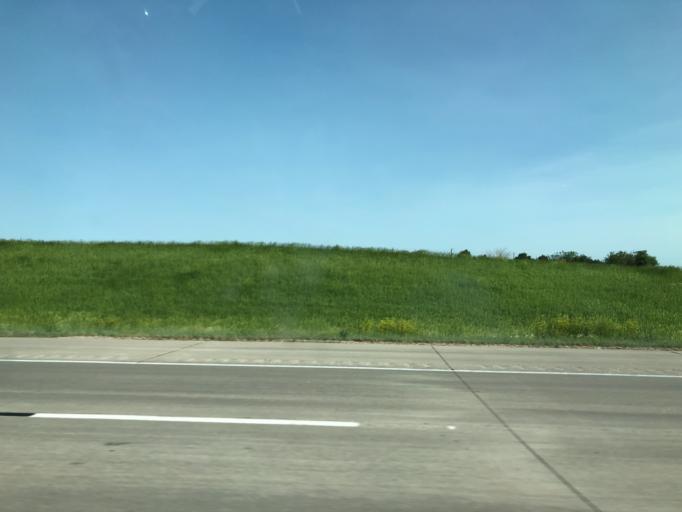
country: US
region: Nebraska
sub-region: Saunders County
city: Ashland
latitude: 40.9949
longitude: -96.3466
